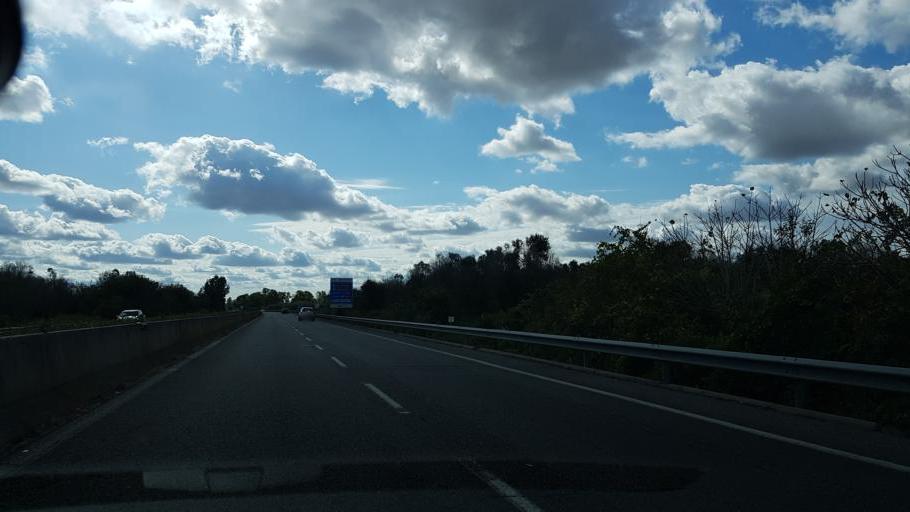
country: IT
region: Apulia
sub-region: Provincia di Brindisi
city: San Pietro Vernotico
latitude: 40.5269
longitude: 18.0127
